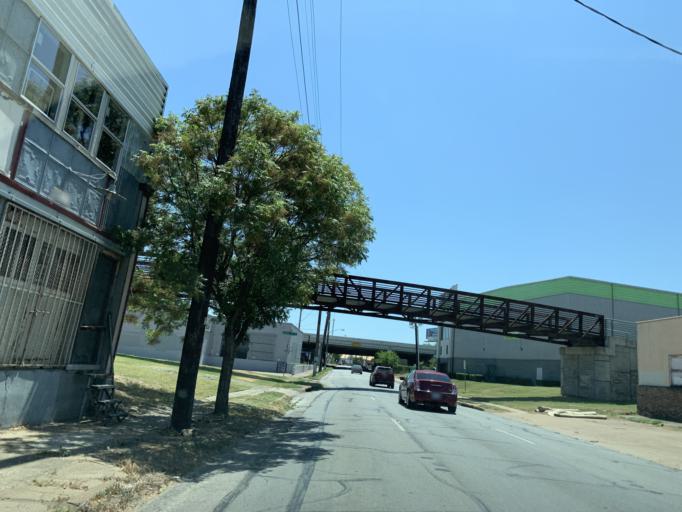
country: US
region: Texas
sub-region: Dallas County
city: Dallas
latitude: 32.7870
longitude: -96.7688
